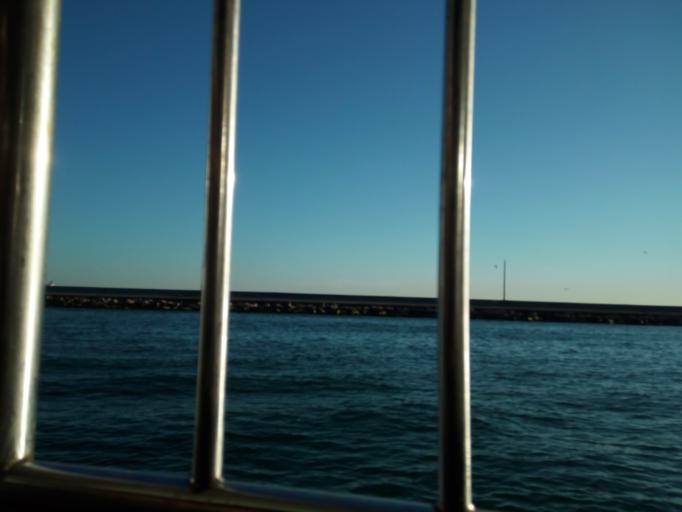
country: TR
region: Istanbul
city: UEskuedar
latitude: 40.9973
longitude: 29.0125
